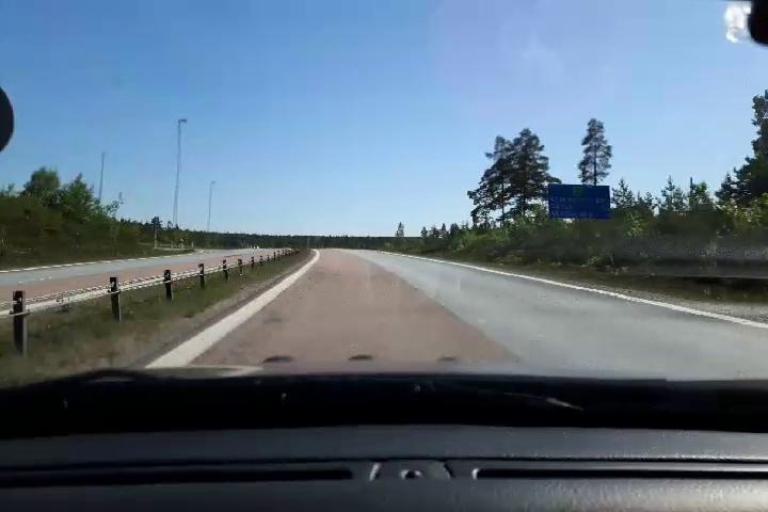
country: SE
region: Gaevleborg
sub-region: Soderhamns Kommun
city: Soderhamn
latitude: 61.3377
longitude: 17.0167
